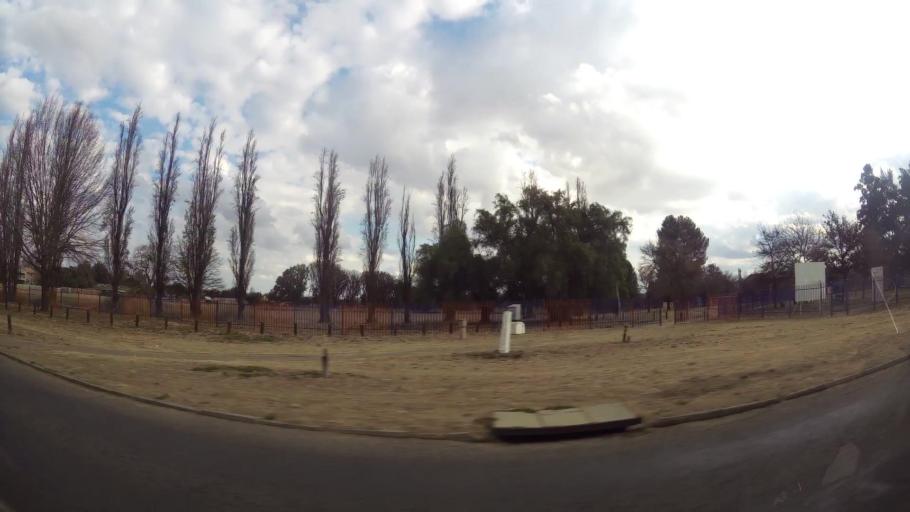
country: ZA
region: Orange Free State
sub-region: Fezile Dabi District Municipality
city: Sasolburg
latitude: -26.8025
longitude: 27.8113
